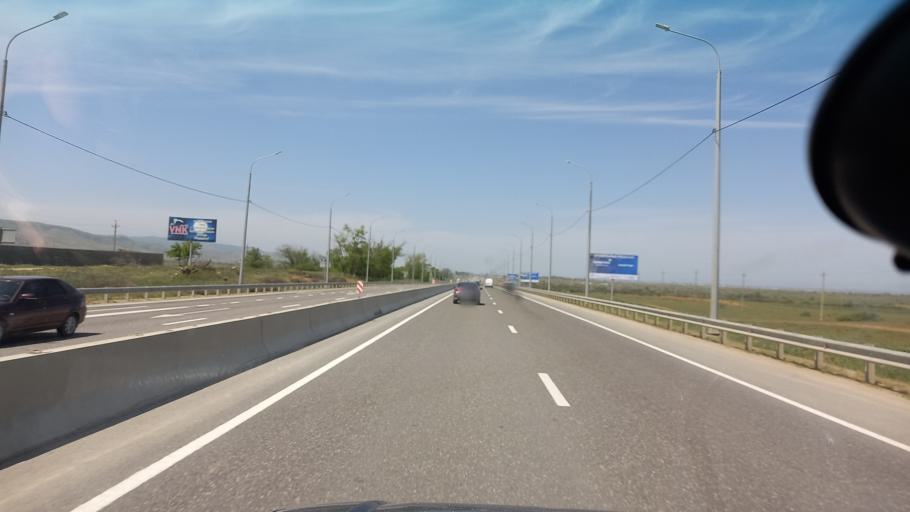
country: RU
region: Dagestan
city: Manas
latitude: 42.7329
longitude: 47.6636
